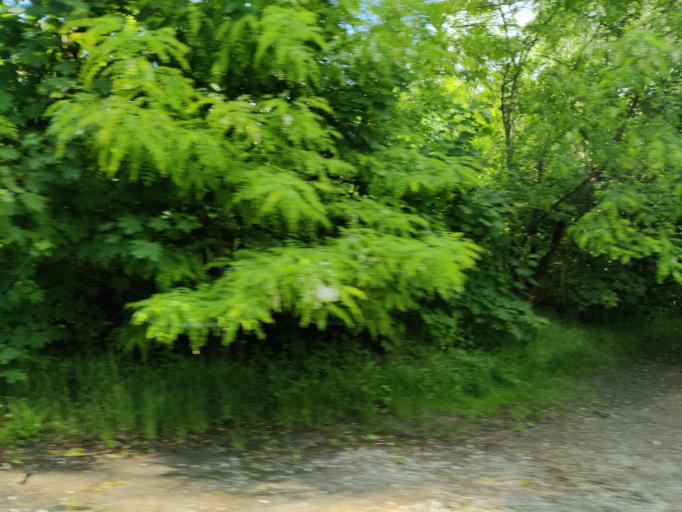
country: PL
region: Masovian Voivodeship
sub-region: Powiat piaseczynski
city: Konstancin-Jeziorna
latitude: 52.1163
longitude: 21.1108
